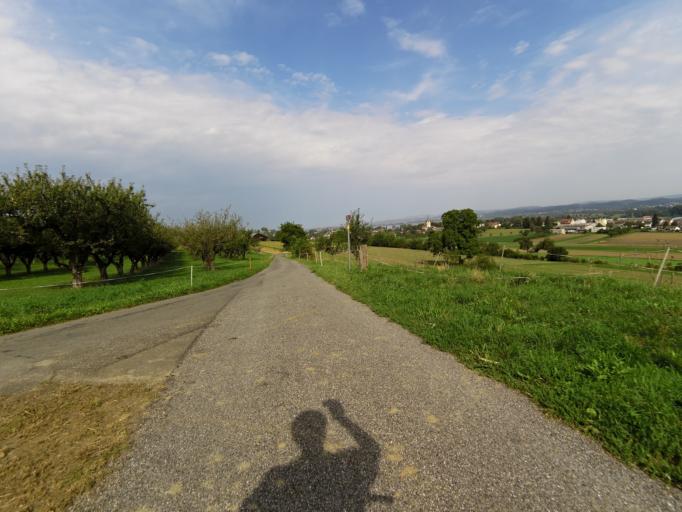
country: CH
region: Thurgau
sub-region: Kreuzlingen District
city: Tagerwilen
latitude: 47.6465
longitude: 9.1449
